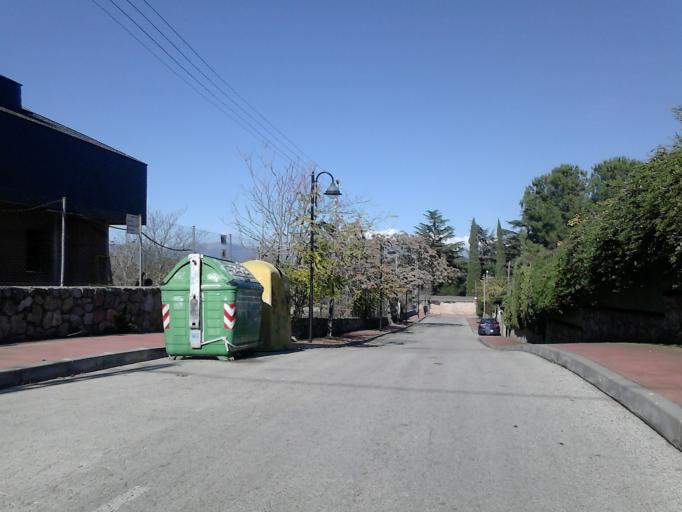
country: ES
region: Madrid
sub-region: Provincia de Madrid
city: Galapagar
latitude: 40.5729
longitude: -3.9958
